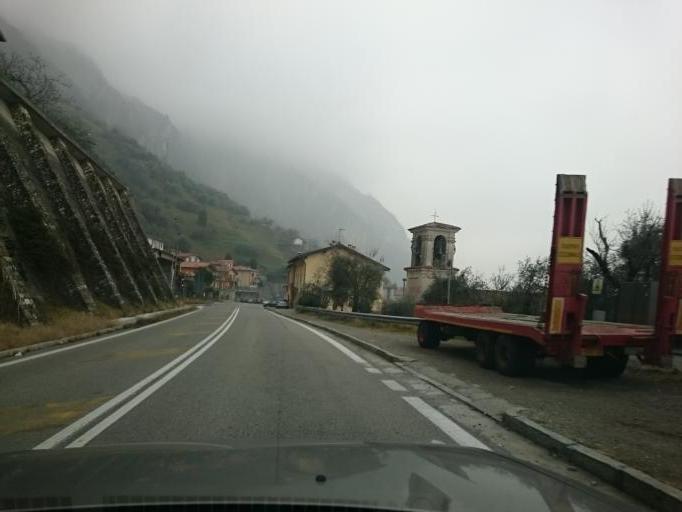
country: IT
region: Lombardy
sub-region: Provincia di Brescia
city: Marone
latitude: 45.7550
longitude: 10.0811
